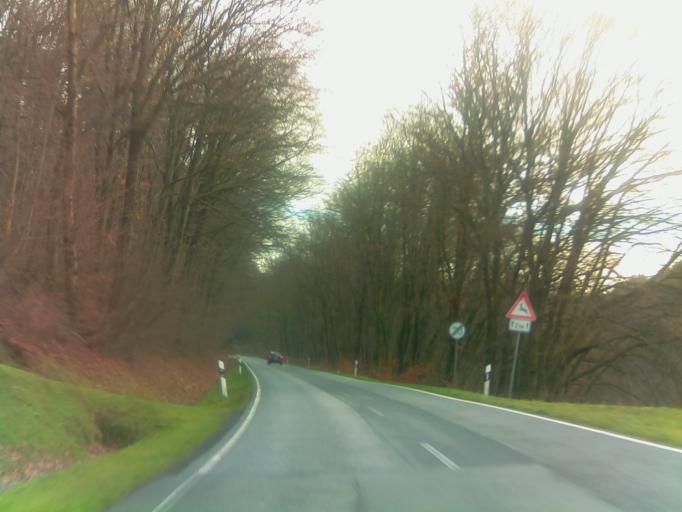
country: DE
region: Hesse
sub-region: Regierungsbezirk Darmstadt
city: Erbach
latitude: 49.6311
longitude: 8.9147
